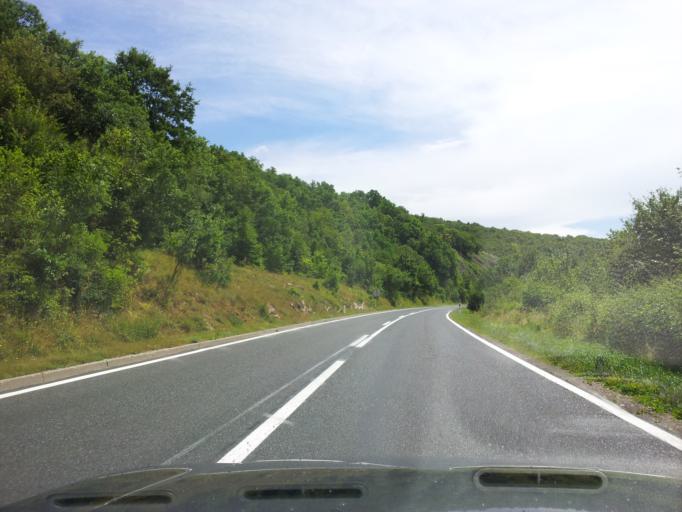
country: BA
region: Federation of Bosnia and Herzegovina
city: Bihac
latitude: 44.6144
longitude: 15.7397
